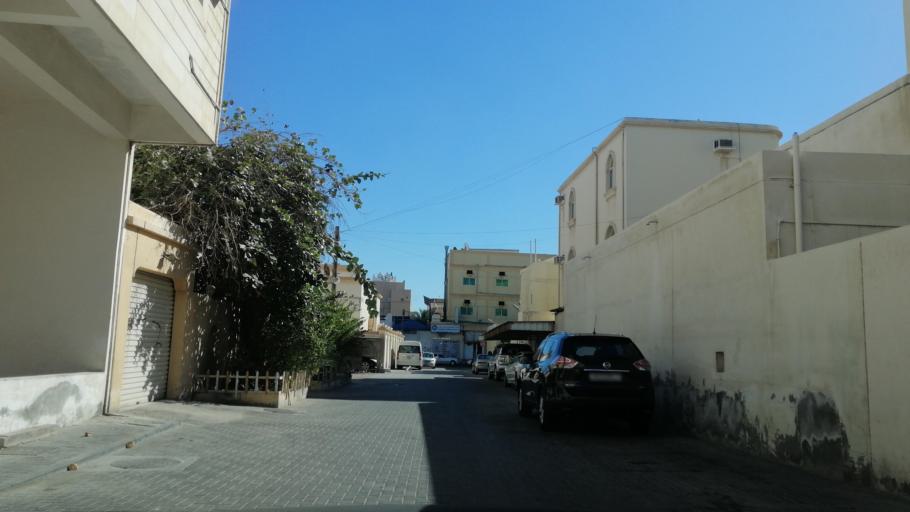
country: BH
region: Muharraq
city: Al Hadd
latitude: 26.2399
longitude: 50.6525
